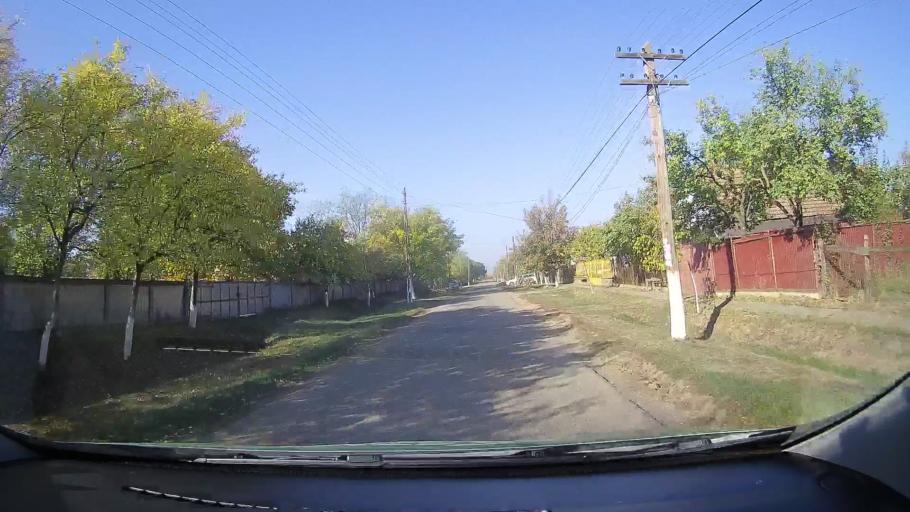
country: RO
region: Satu Mare
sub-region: Comuna Sauca
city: Sauca
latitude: 47.4690
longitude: 22.4981
